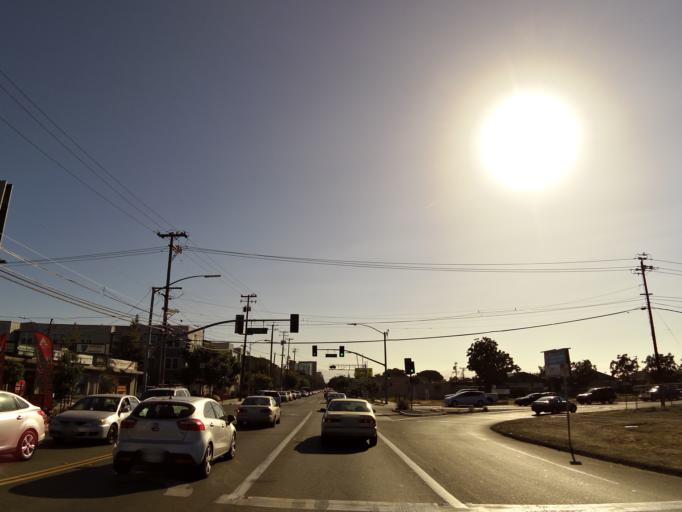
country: US
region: California
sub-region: Santa Clara County
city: San Jose
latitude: 37.3582
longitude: -121.8934
